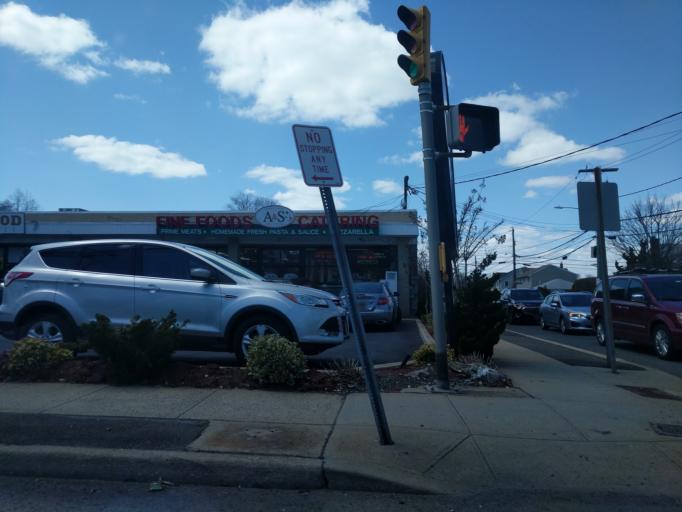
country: US
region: New York
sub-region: Nassau County
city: Oceanside
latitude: 40.6286
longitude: -73.6411
